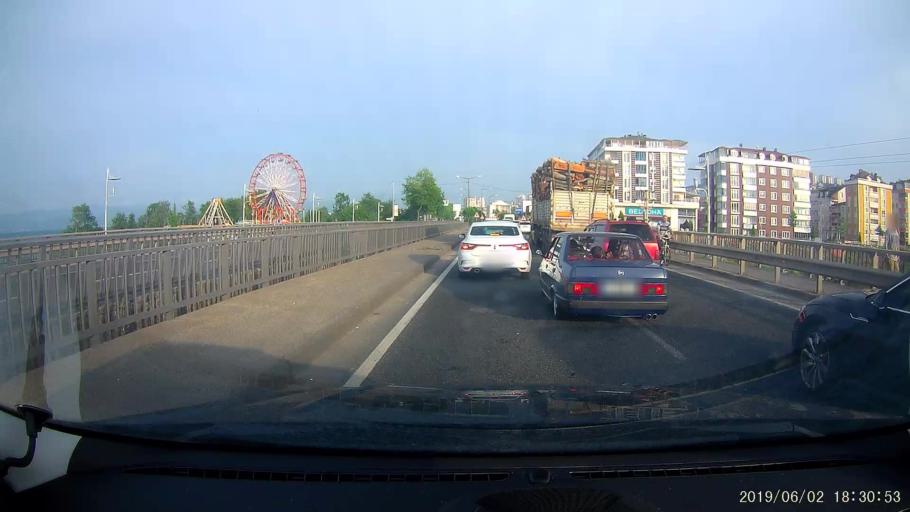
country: TR
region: Ordu
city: Fatsa
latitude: 41.0374
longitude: 37.4922
